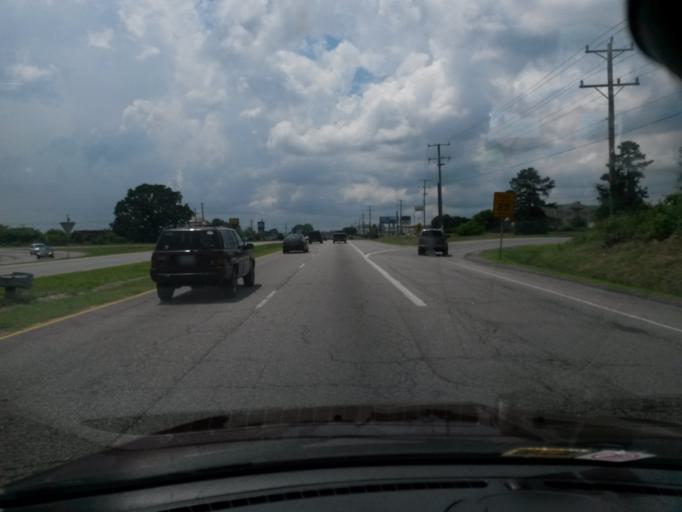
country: US
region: Virginia
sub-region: Chesterfield County
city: Chester
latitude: 37.3547
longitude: -77.4055
